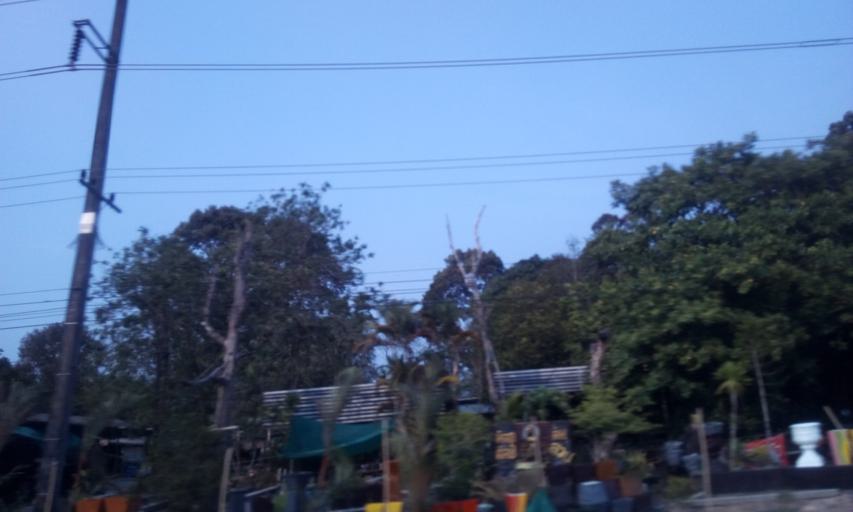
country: TH
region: Chanthaburi
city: Khlung
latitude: 12.4358
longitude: 102.3067
